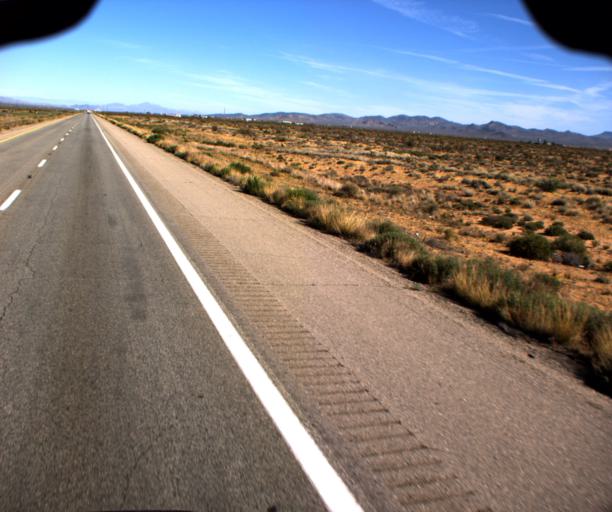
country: US
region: Arizona
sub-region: Mohave County
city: Dolan Springs
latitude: 35.5097
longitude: -114.3384
